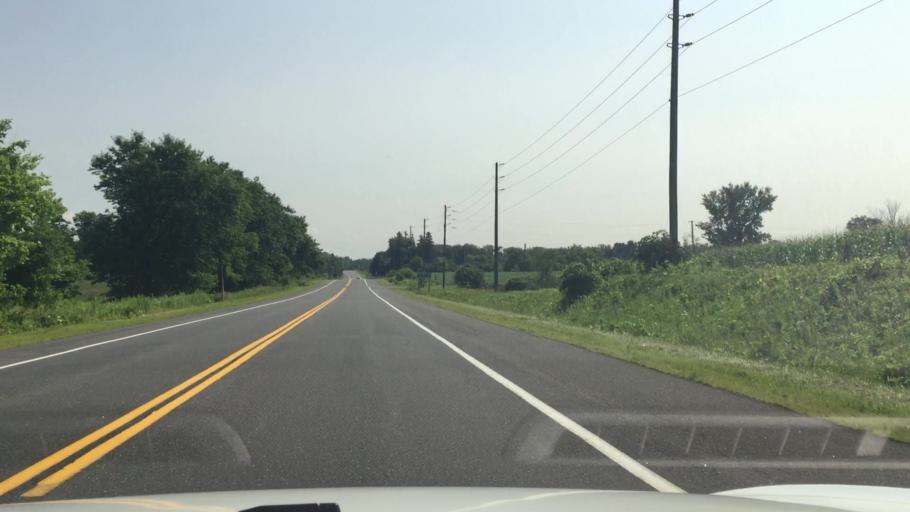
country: CA
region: Ontario
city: Pickering
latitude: 43.9139
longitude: -79.1279
